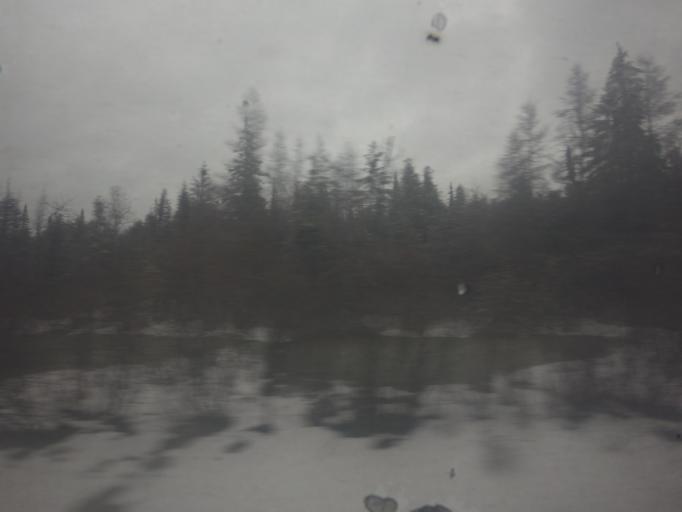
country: CA
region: Ontario
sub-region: Lanark County
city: Smiths Falls
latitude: 45.0275
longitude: -75.9366
